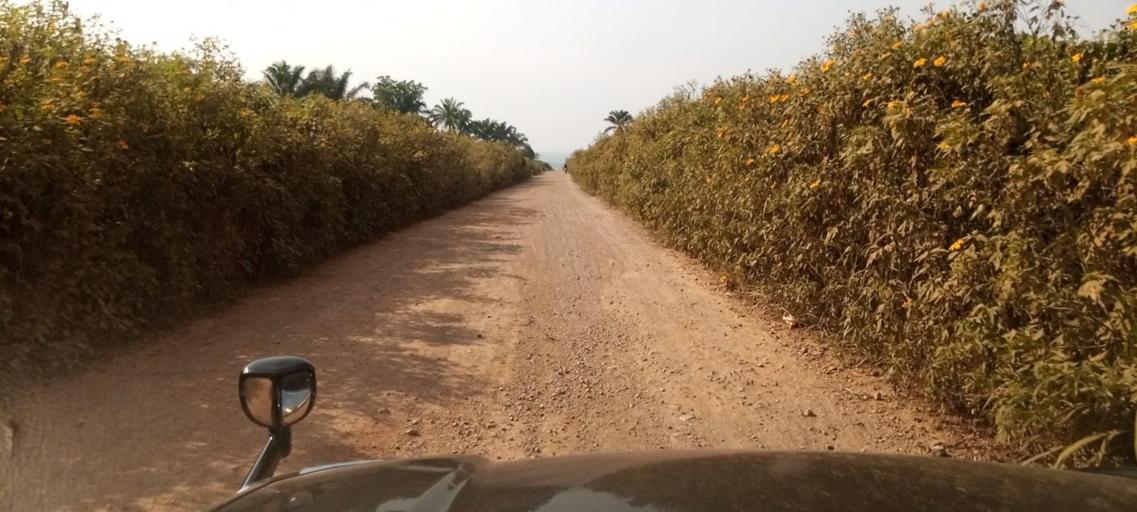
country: CD
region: Kasai-Oriental
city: Mbuji-Mayi
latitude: -6.3649
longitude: 23.8213
